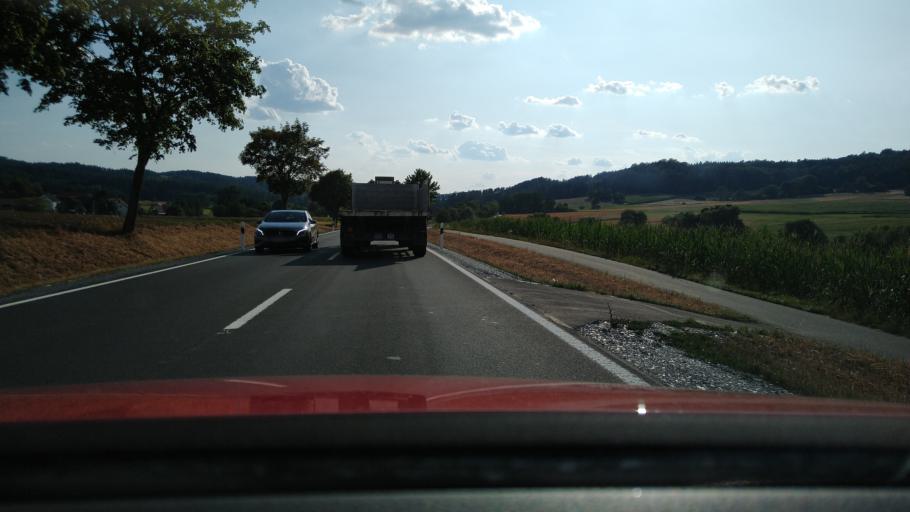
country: DE
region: Bavaria
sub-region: Upper Franconia
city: Mistelgau
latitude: 49.9277
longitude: 11.4532
